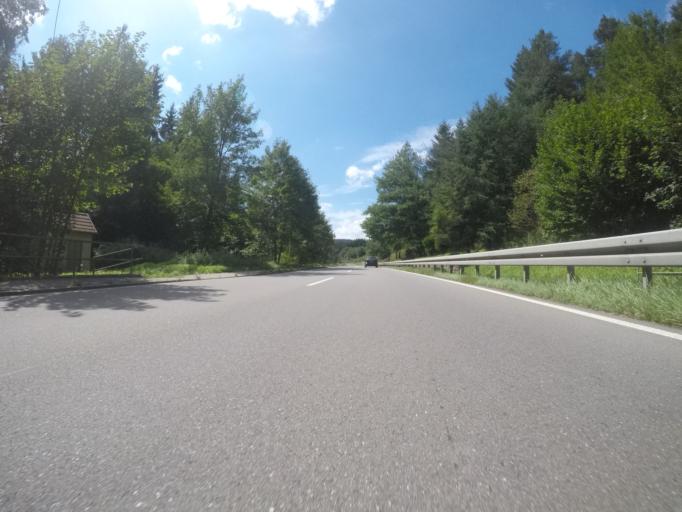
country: DE
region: Baden-Wuerttemberg
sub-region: Karlsruhe Region
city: Ebhausen
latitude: 48.5897
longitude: 8.6687
